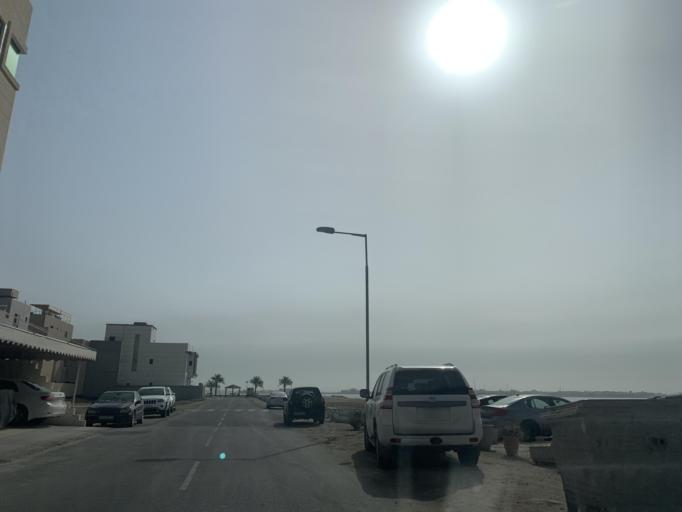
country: BH
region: Northern
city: Madinat `Isa
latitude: 26.1867
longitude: 50.5657
